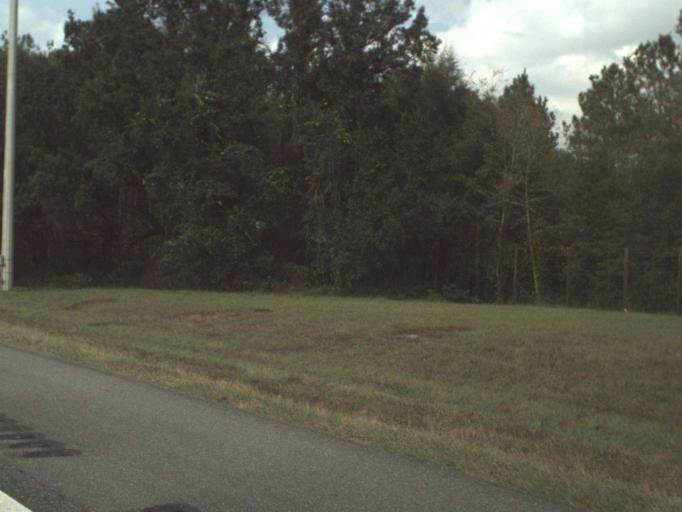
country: US
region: Florida
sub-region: Gadsden County
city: Quincy
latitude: 30.5307
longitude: -84.5350
